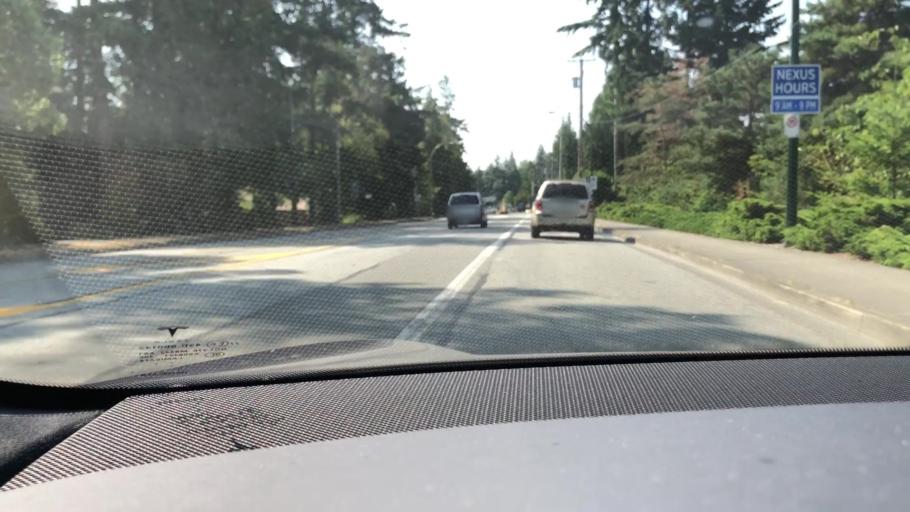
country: US
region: Washington
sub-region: Whatcom County
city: Point Roberts
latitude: 49.0040
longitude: -123.0687
